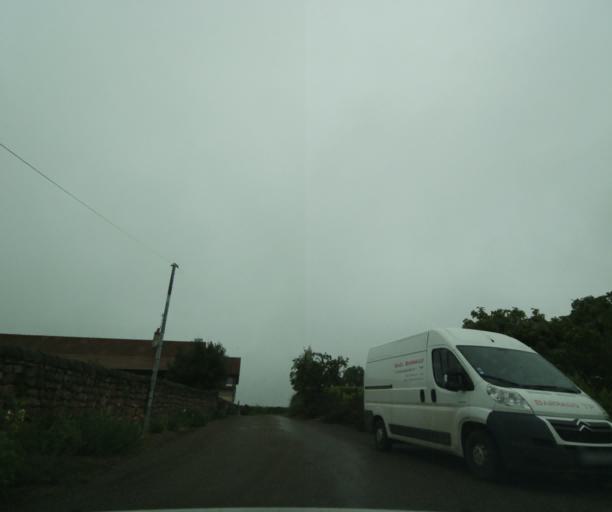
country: FR
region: Bourgogne
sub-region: Departement de Saone-et-Loire
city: Charolles
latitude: 46.4003
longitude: 4.3852
